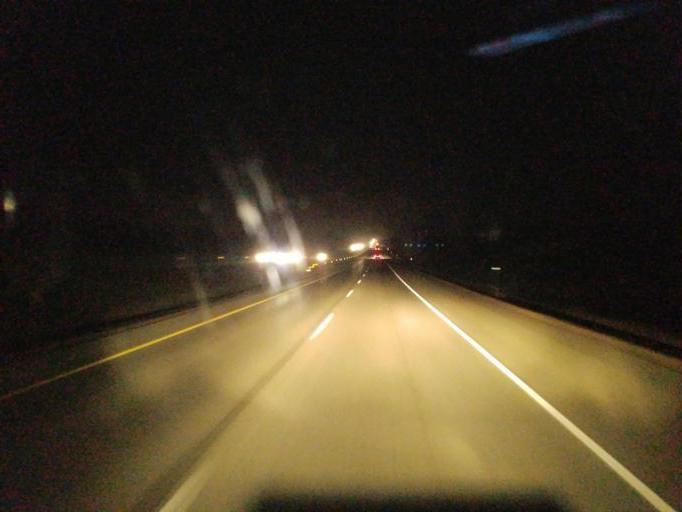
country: US
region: Iowa
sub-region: Madison County
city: Earlham
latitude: 41.5177
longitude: -94.1671
